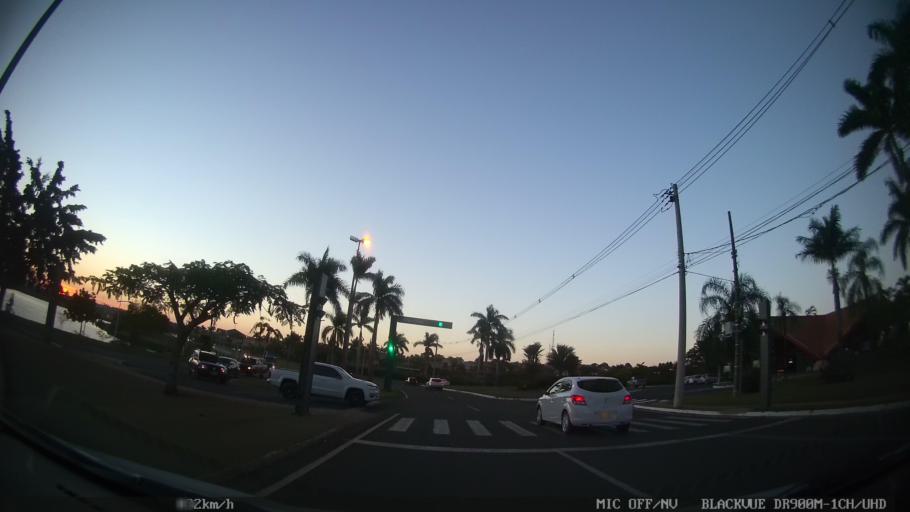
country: BR
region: Sao Paulo
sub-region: Sao Jose Do Rio Preto
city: Sao Jose do Rio Preto
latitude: -20.8127
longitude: -49.3481
